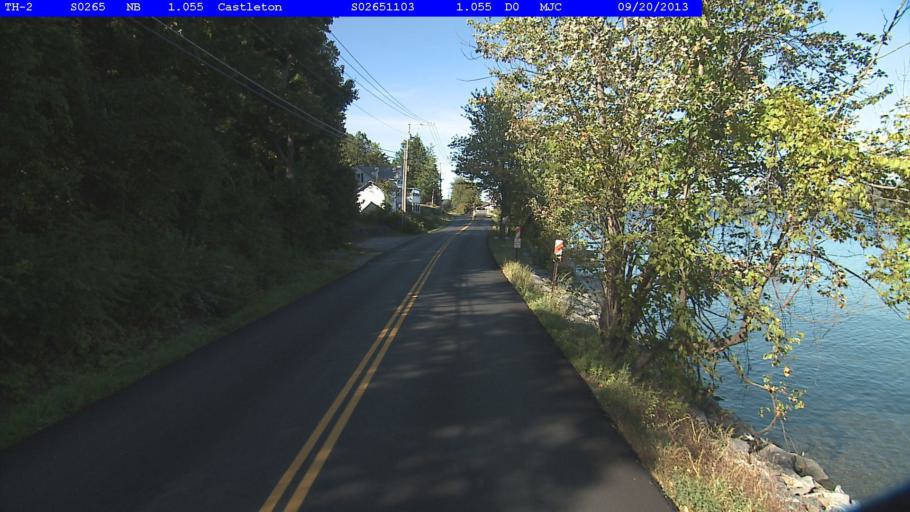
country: US
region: Vermont
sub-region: Rutland County
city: Fair Haven
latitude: 43.6191
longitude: -73.2302
